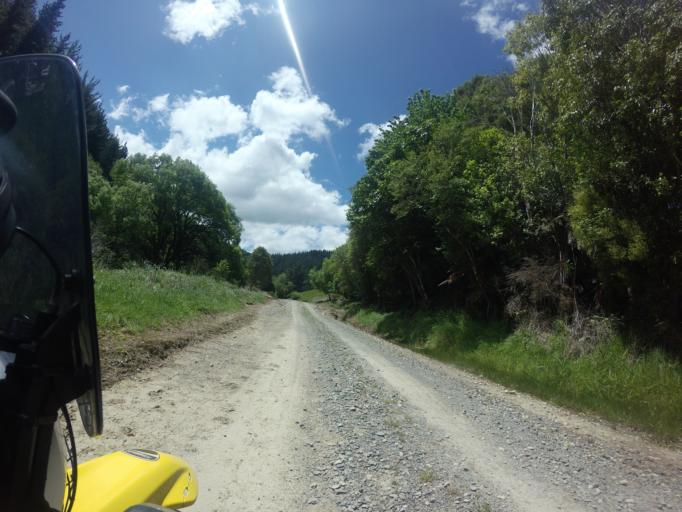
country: NZ
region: Hawke's Bay
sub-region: Wairoa District
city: Wairoa
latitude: -38.9738
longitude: 177.6799
